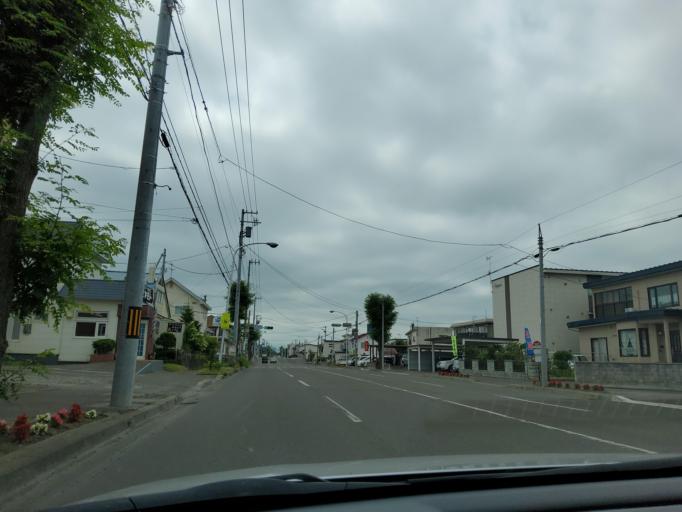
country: JP
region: Hokkaido
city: Obihiro
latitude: 42.9153
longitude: 143.1832
